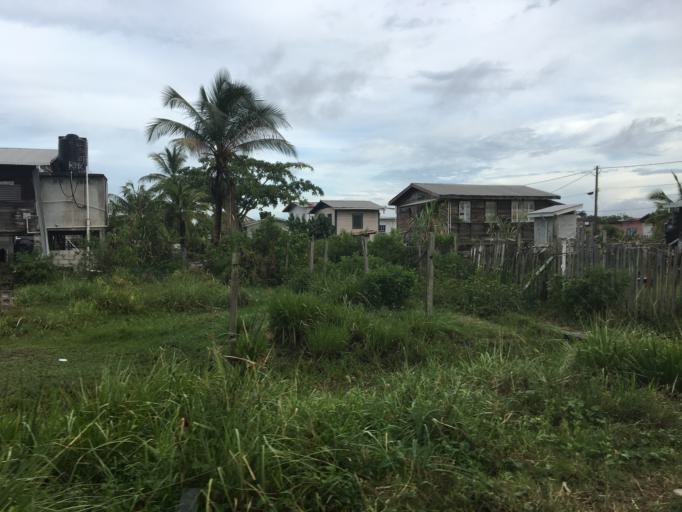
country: GY
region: Demerara-Mahaica
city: Georgetown
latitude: 6.7987
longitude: -58.1213
